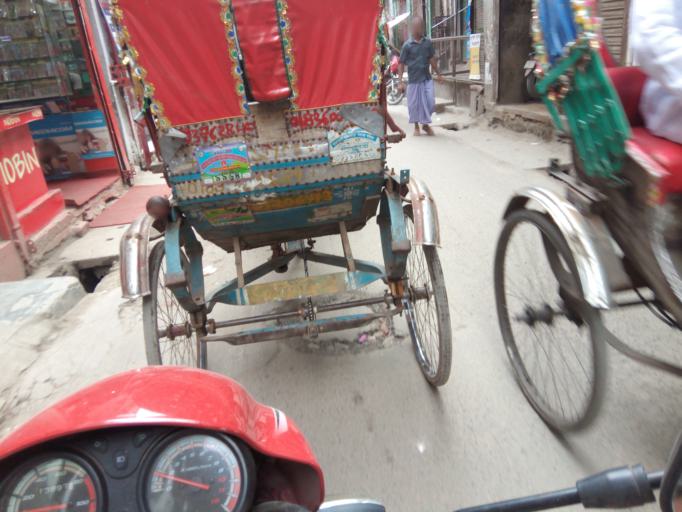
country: BD
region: Dhaka
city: Azimpur
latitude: 23.7188
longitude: 90.3912
